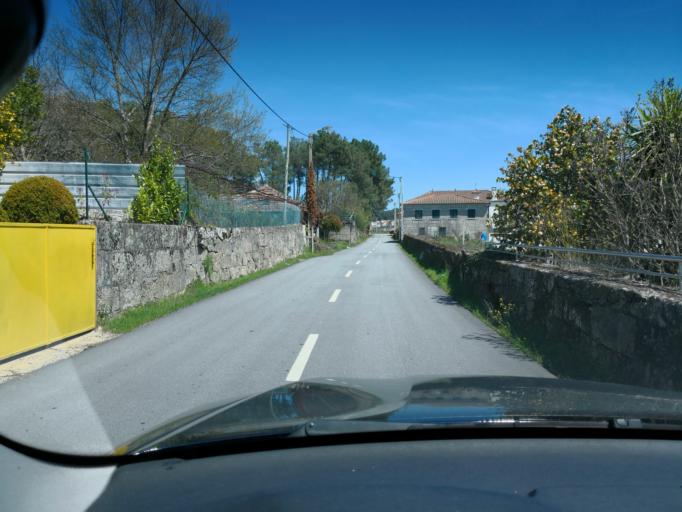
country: PT
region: Vila Real
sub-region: Vila Real
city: Vila Real
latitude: 41.3191
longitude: -7.6831
